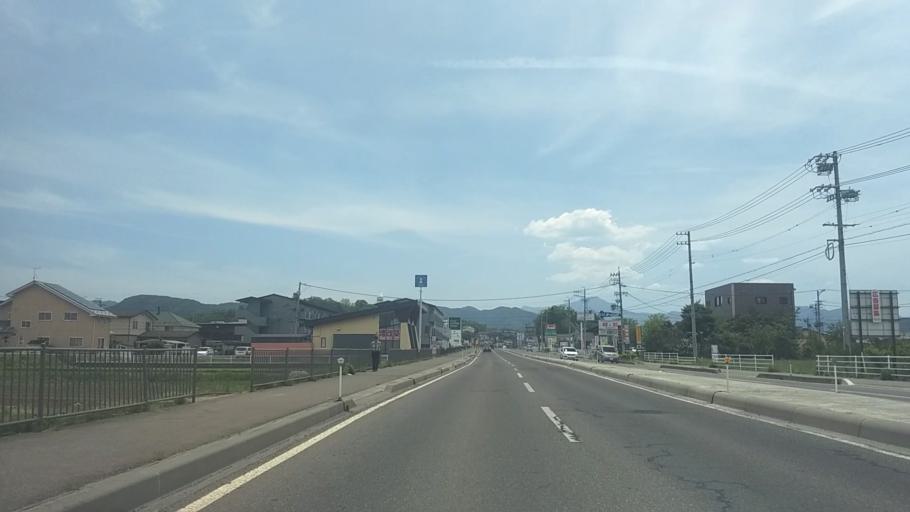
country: JP
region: Nagano
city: Saku
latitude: 36.1969
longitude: 138.4749
